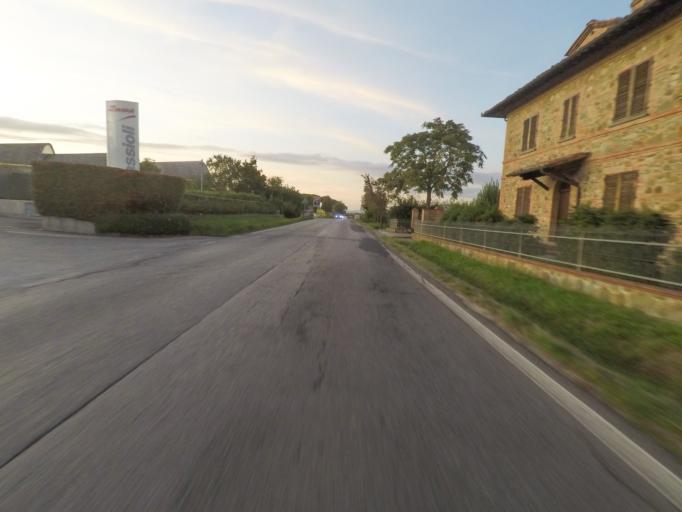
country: IT
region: Tuscany
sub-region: Provincia di Siena
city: Torrita di Siena
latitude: 43.1803
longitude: 11.7711
